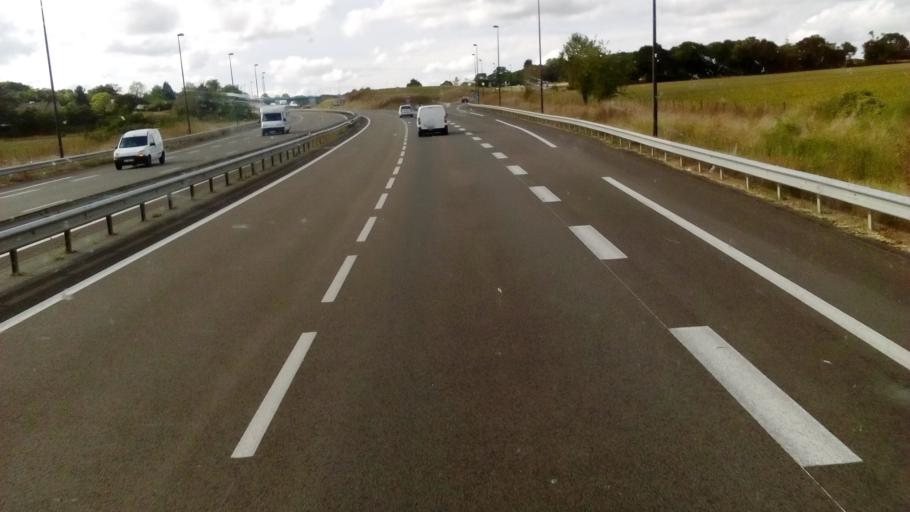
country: FR
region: Bourgogne
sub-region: Departement de la Nievre
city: Varennes-Vauzelles
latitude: 47.0333
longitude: 3.1502
